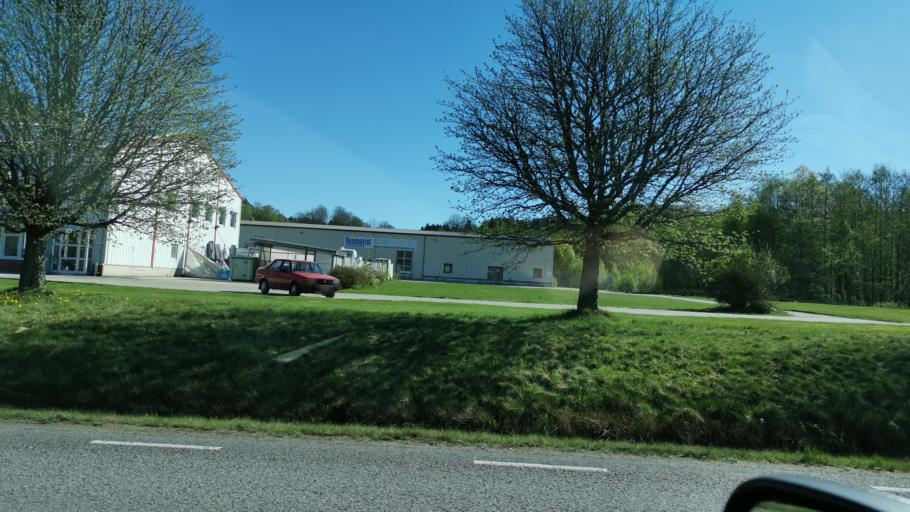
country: SE
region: Vaestra Goetaland
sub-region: Uddevalla Kommun
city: Ljungskile
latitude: 58.2385
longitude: 11.9149
